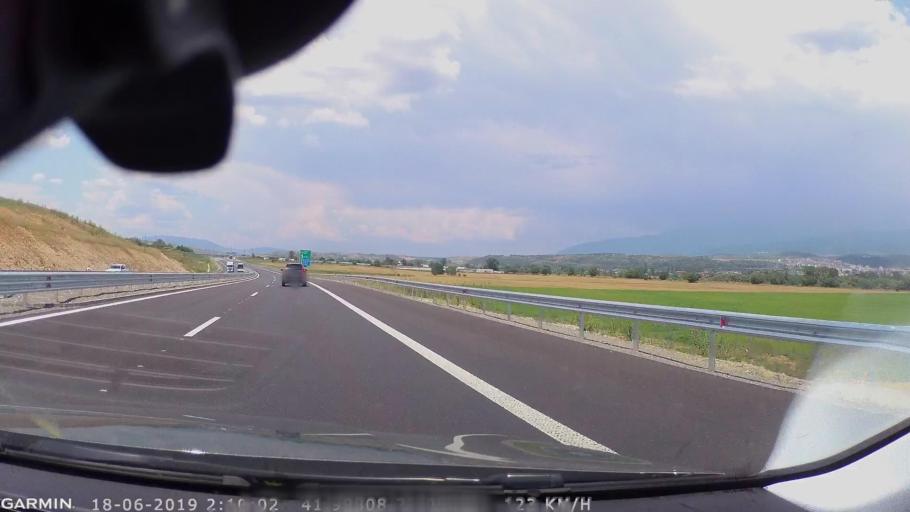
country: BG
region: Blagoevgrad
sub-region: Obshtina Blagoevgrad
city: Blagoevgrad
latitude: 41.9810
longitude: 23.0629
